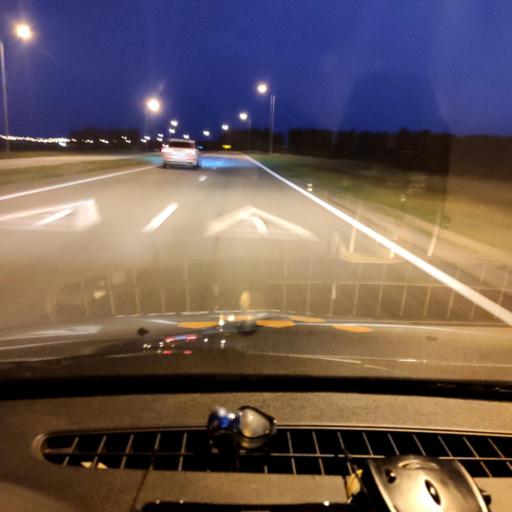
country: RU
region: Belgorod
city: Skorodnoye
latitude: 51.0765
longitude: 37.2081
